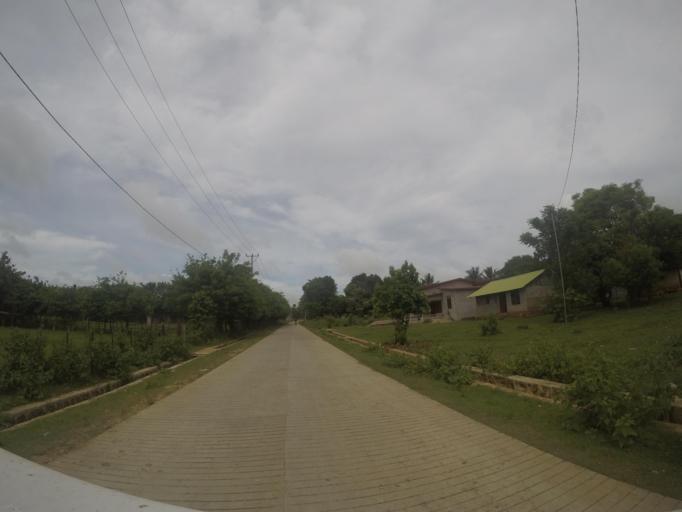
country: TL
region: Lautem
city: Lospalos
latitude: -8.5087
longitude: 126.9837
